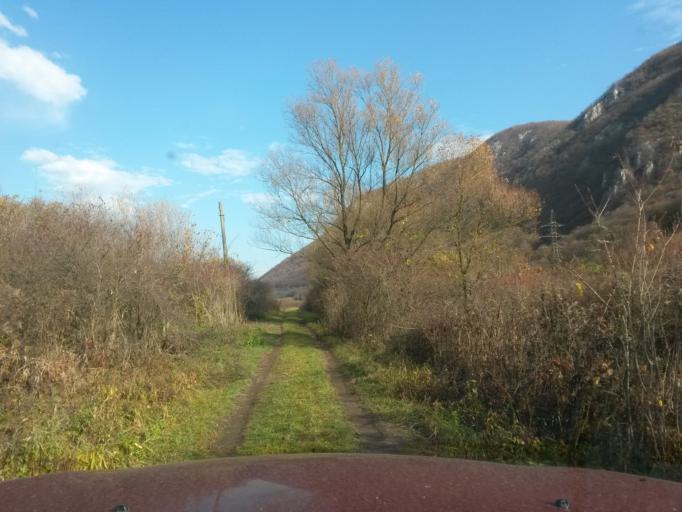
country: SK
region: Kosicky
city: Roznava
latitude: 48.5894
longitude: 20.4806
